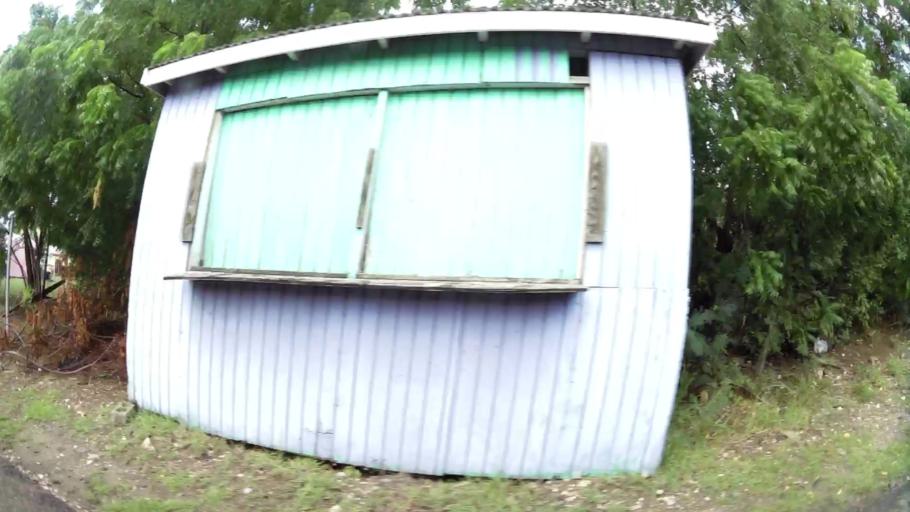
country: AG
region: Saint Mary
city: Bolands
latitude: 17.0673
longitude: -61.8717
